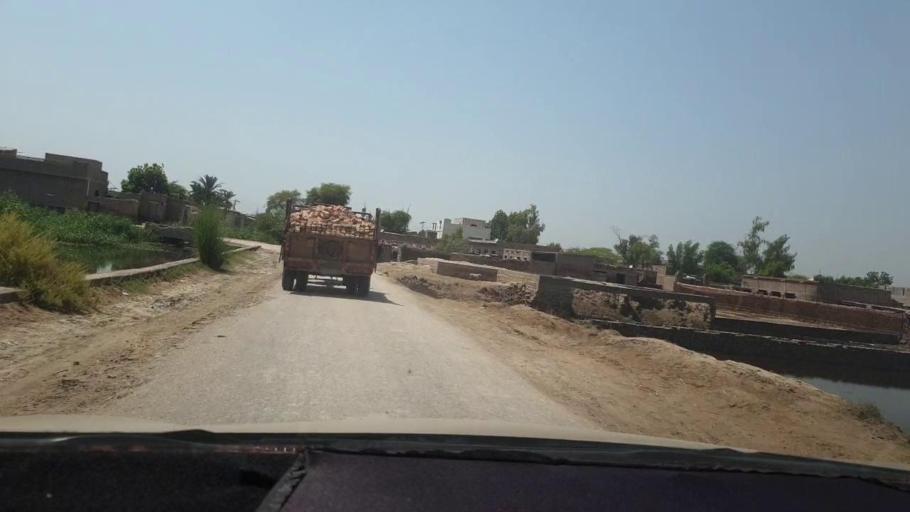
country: PK
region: Sindh
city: Shahdadkot
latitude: 27.8272
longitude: 67.9214
